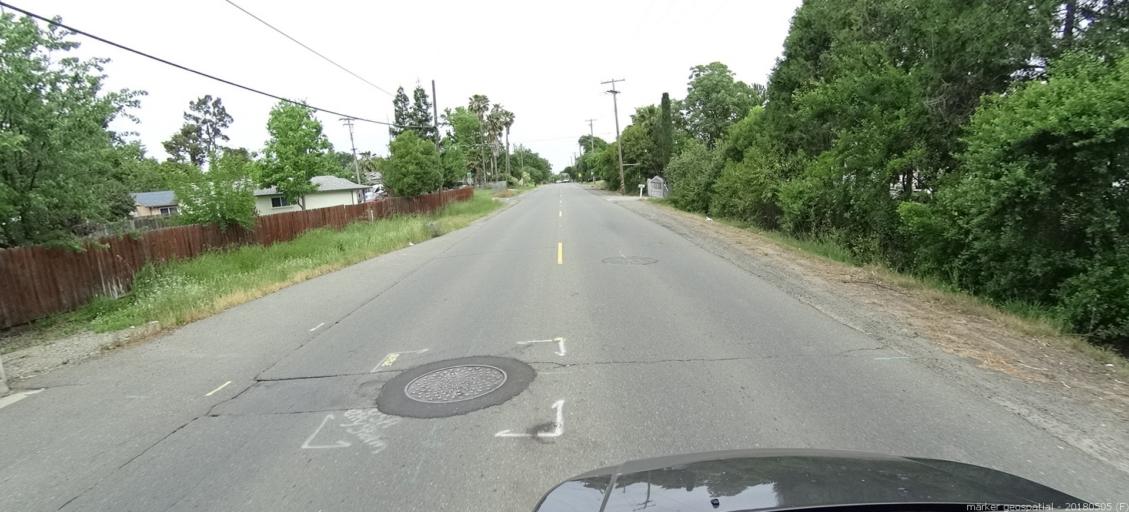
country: US
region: California
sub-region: Sacramento County
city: Rio Linda
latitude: 38.6593
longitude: -121.4448
